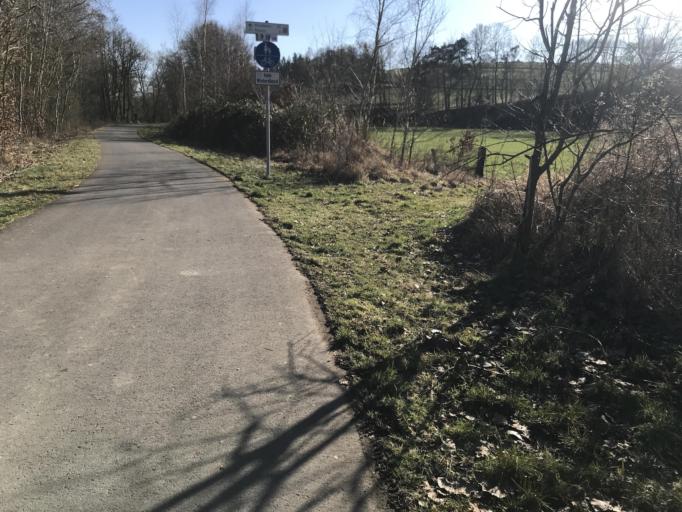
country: DE
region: Hesse
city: Neukirchen
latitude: 50.8608
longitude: 9.3508
